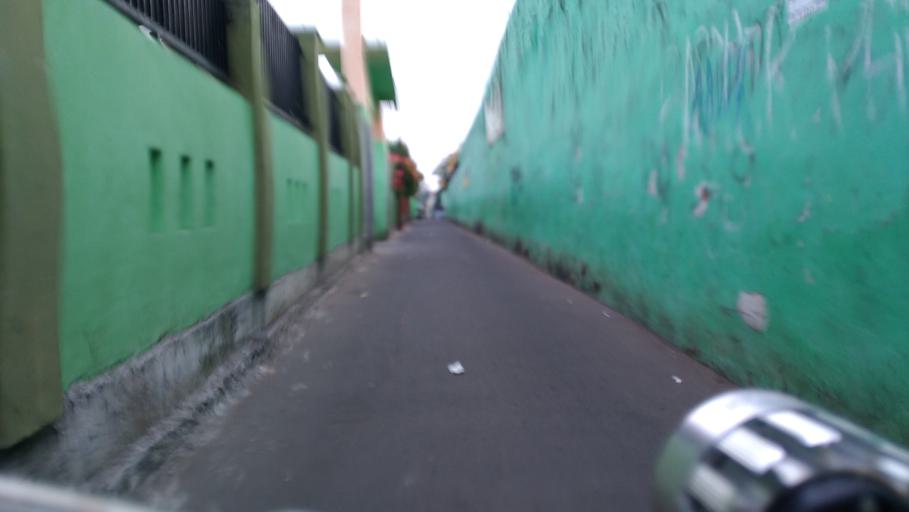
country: ID
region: West Java
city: Depok
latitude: -6.3517
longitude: 106.8663
